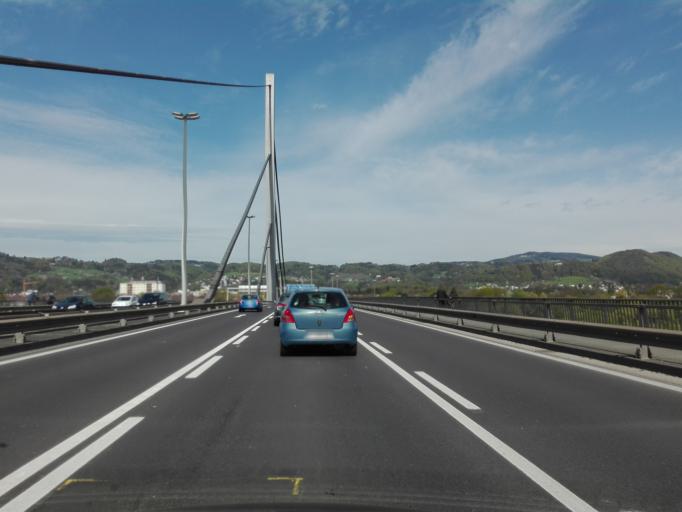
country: AT
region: Upper Austria
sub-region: Linz Stadt
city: Linz
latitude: 48.3190
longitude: 14.3003
